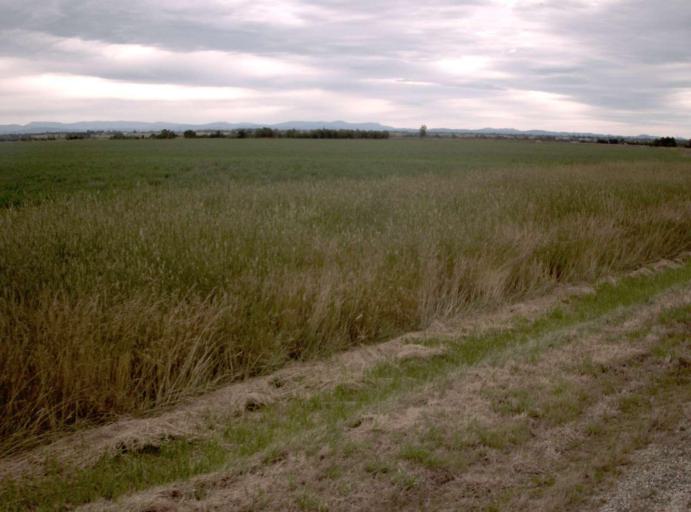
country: AU
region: Victoria
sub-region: Wellington
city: Sale
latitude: -38.0478
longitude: 147.1746
